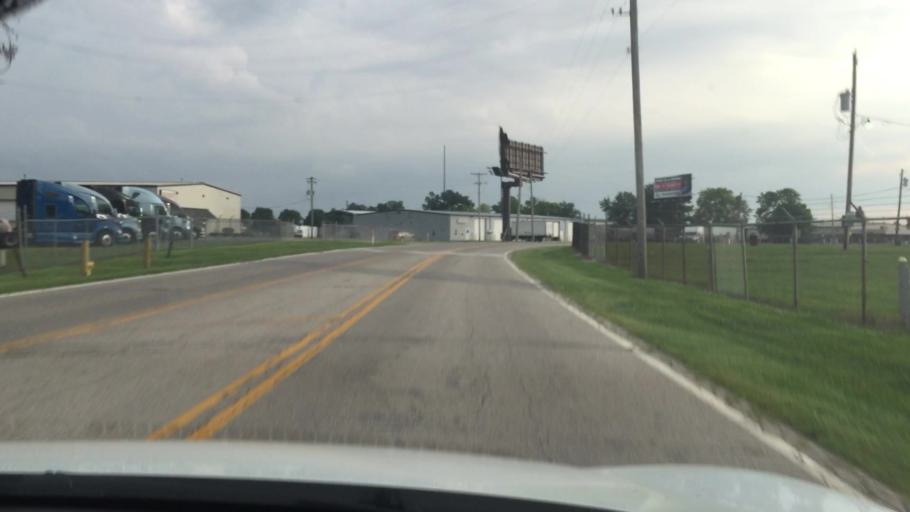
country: US
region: Ohio
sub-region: Clark County
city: Springfield
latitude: 39.8954
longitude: -83.7296
